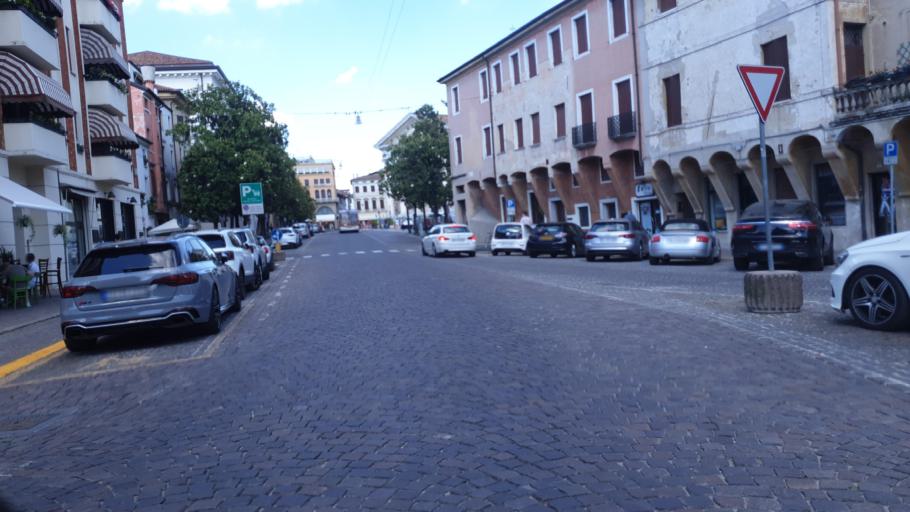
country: IT
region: Veneto
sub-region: Provincia di Treviso
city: Treviso
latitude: 45.6658
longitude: 12.2413
